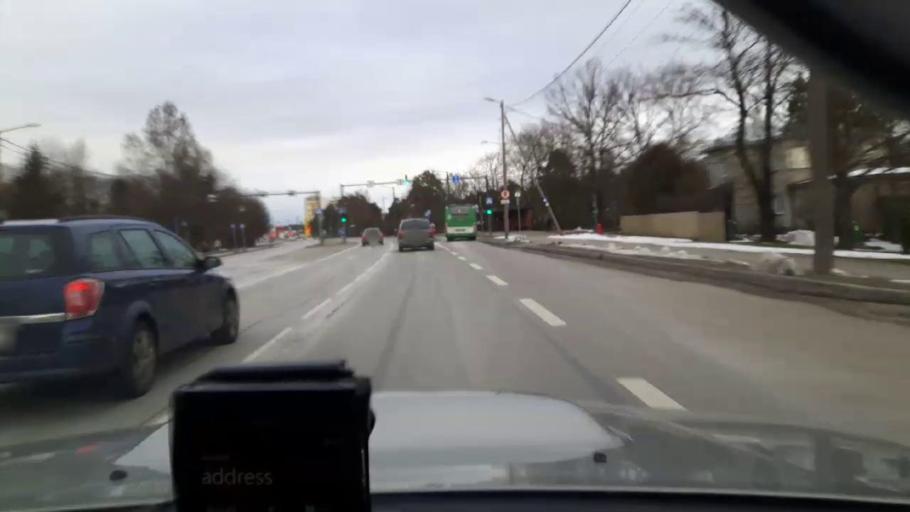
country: EE
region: Harju
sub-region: Saue vald
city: Laagri
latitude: 59.3554
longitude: 24.6309
